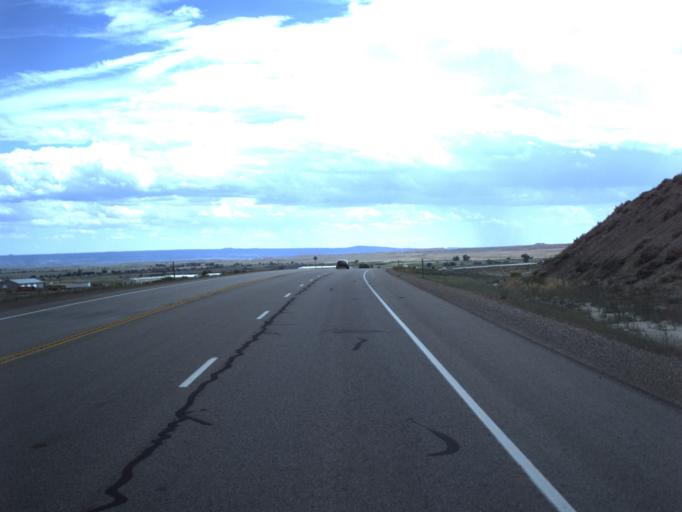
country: US
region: Utah
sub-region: Carbon County
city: Price
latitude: 39.5436
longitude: -110.8149
